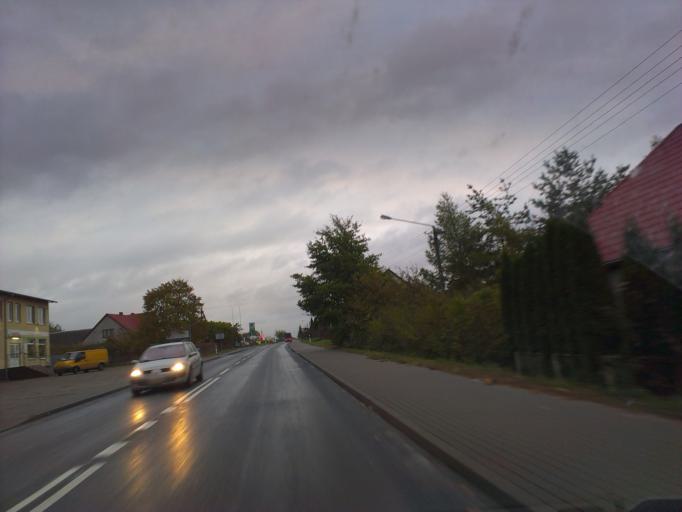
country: PL
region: Kujawsko-Pomorskie
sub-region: Powiat tucholski
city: Lubiewo
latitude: 53.5051
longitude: 18.0047
